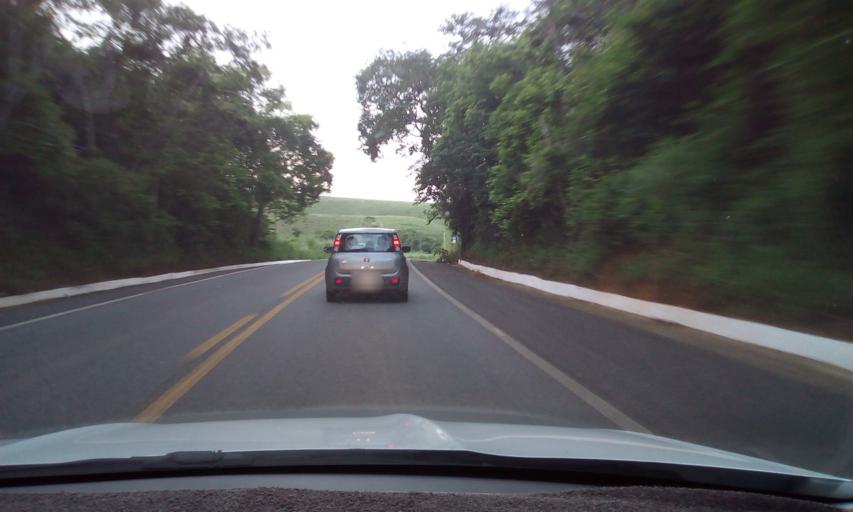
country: BR
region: Pernambuco
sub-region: Vicencia
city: Vicencia
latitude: -7.6432
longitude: -35.2543
